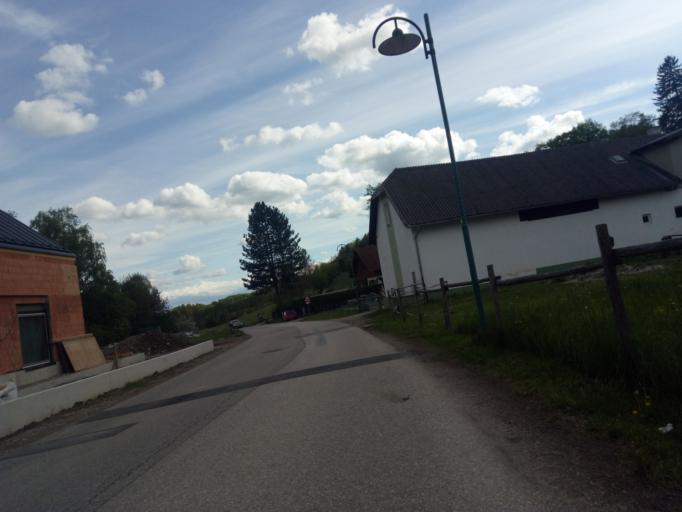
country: AT
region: Lower Austria
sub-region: Politischer Bezirk Wien-Umgebung
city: Wolfsgraben
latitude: 48.1276
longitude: 16.0959
